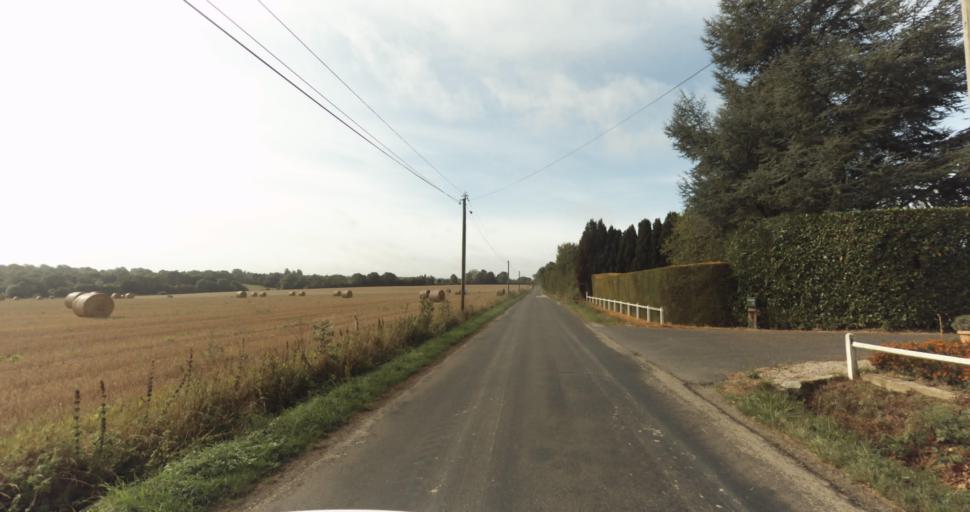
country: FR
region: Lower Normandy
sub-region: Departement de l'Orne
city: Gace
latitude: 48.9042
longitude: 0.3396
